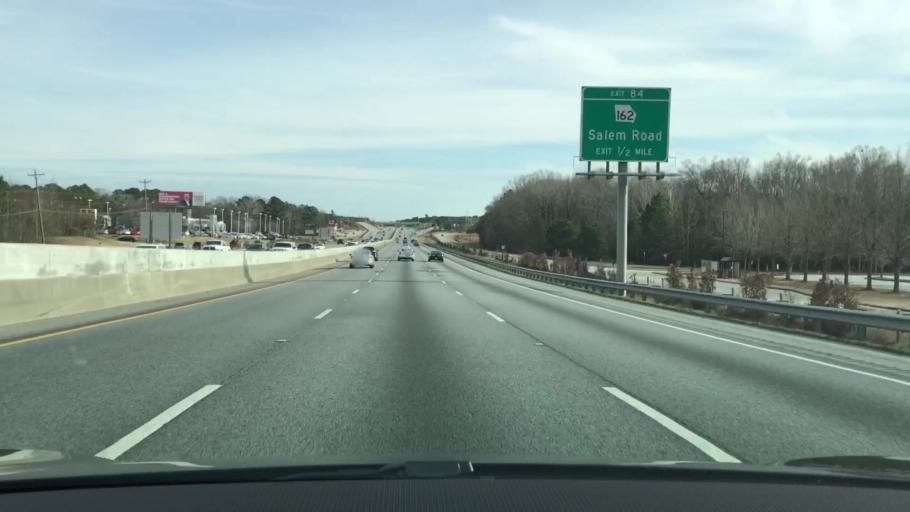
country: US
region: Georgia
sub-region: Rockdale County
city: Conyers
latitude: 33.6421
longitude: -83.9875
